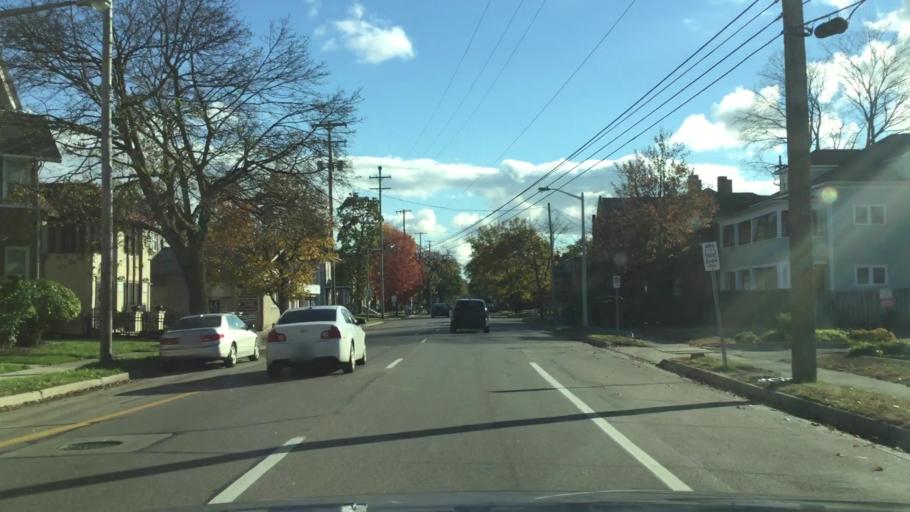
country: US
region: Michigan
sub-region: Kalamazoo County
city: Kalamazoo
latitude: 42.2883
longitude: -85.5895
